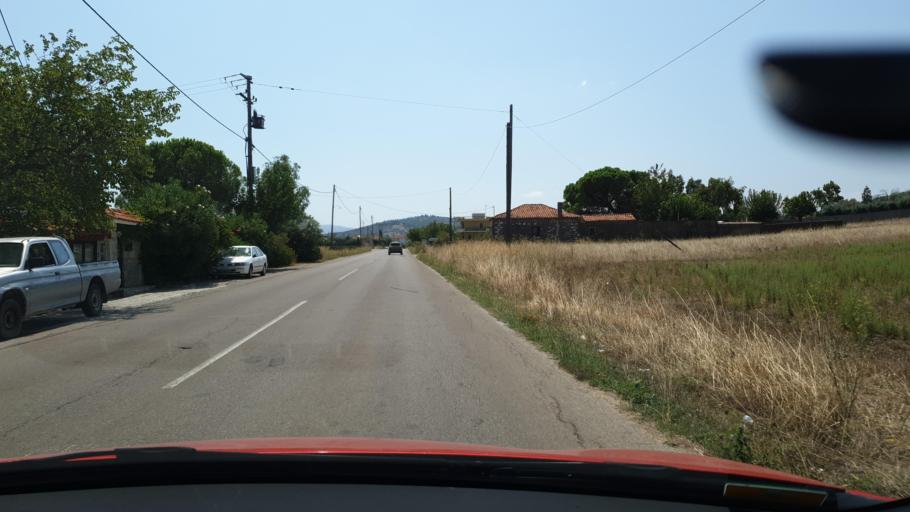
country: GR
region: Central Greece
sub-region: Nomos Evvoias
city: Aliveri
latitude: 38.4610
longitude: 24.1166
